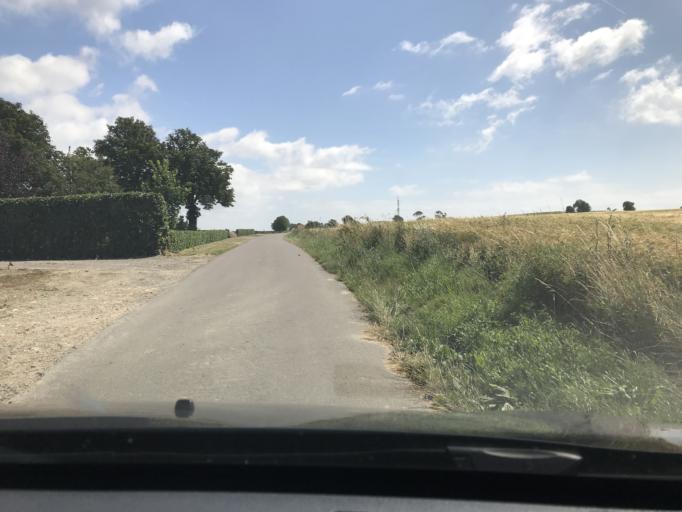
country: DK
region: South Denmark
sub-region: AEro Kommune
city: AEroskobing
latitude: 54.9063
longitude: 10.3031
